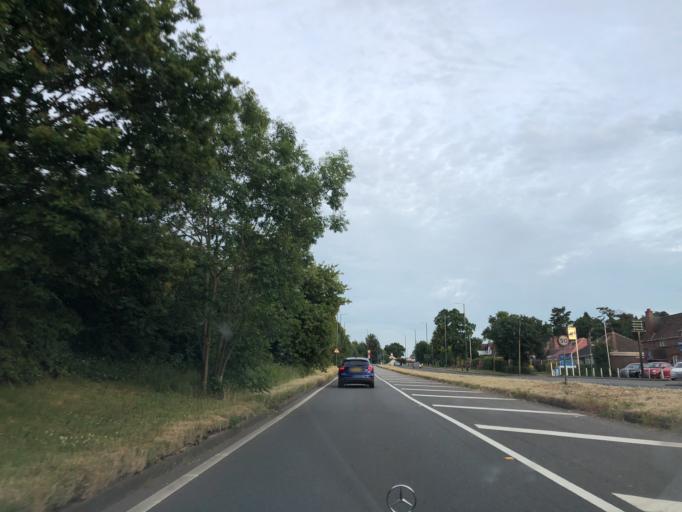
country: GB
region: England
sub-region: Solihull
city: Balsall Common
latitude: 52.4020
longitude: -1.6574
